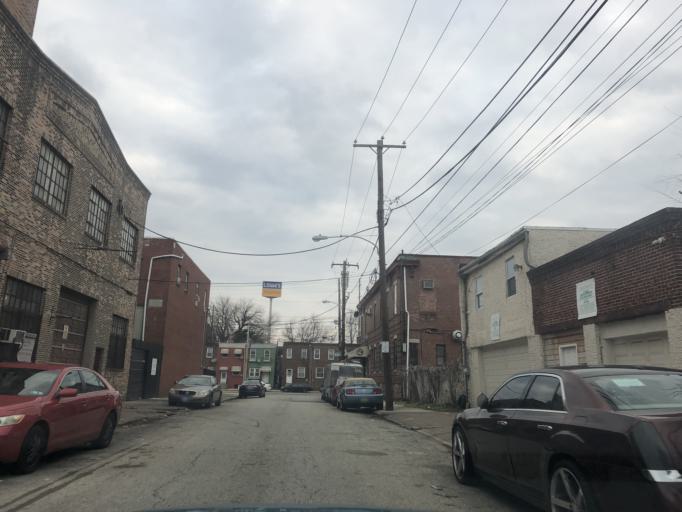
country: US
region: Pennsylvania
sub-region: Delaware County
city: Millbourne
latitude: 39.9752
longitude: -75.2240
